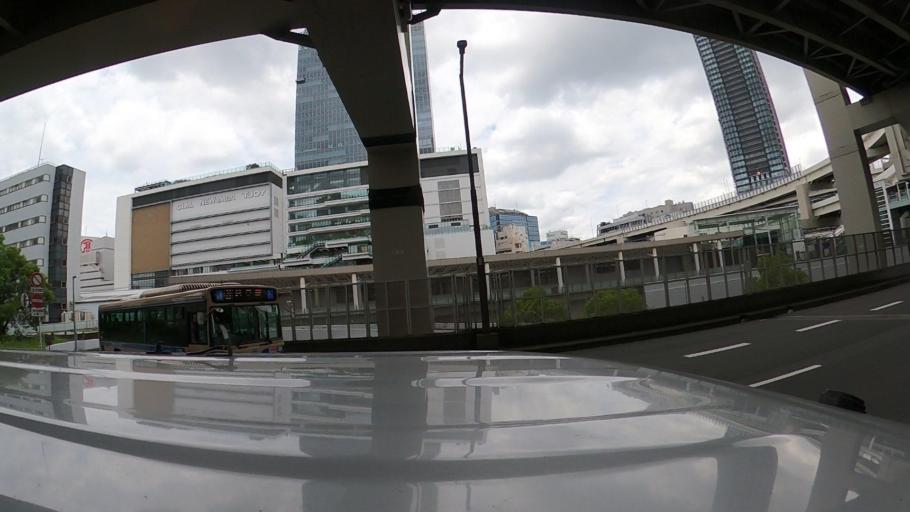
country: JP
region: Kanagawa
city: Yokohama
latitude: 35.4660
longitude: 139.6244
